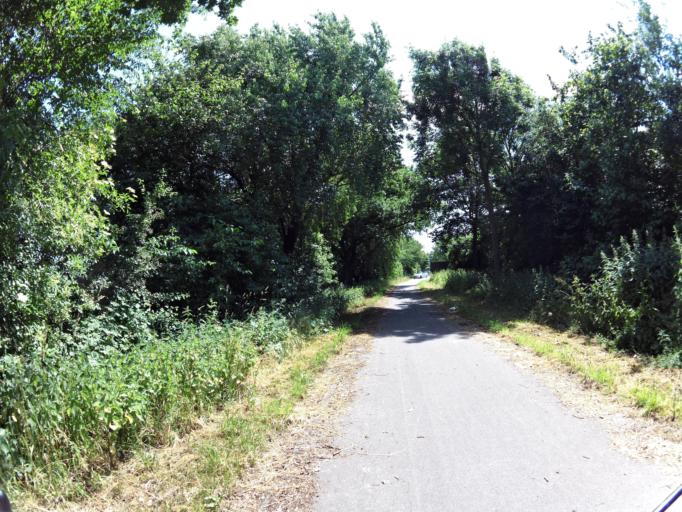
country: DE
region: North Rhine-Westphalia
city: Geilenkirchen
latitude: 51.0078
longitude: 6.1193
